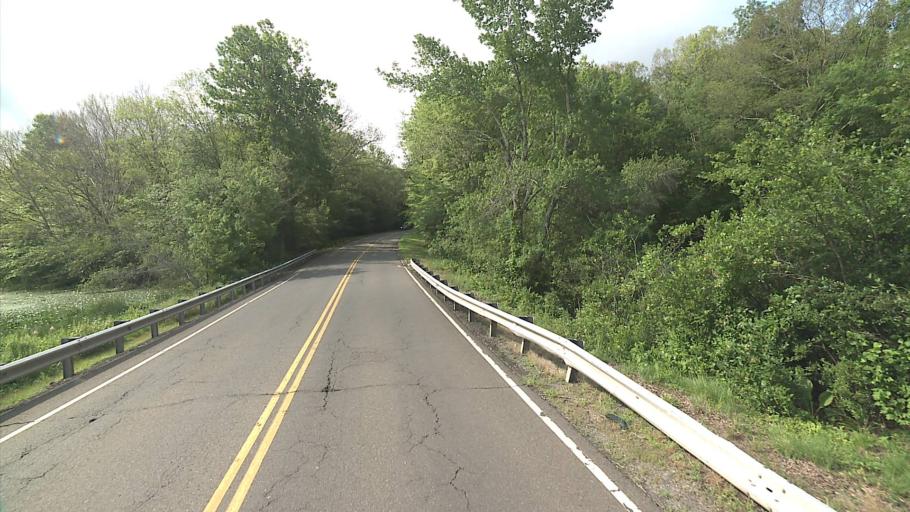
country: US
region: Connecticut
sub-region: Middlesex County
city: Deep River Center
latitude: 41.3397
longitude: -72.4935
